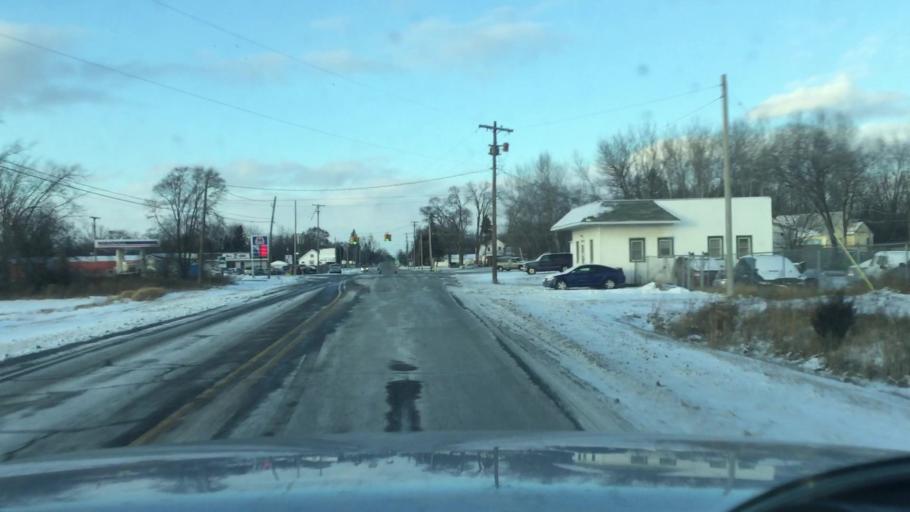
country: US
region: Michigan
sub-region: Saginaw County
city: Saginaw
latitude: 43.3899
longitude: -83.9357
